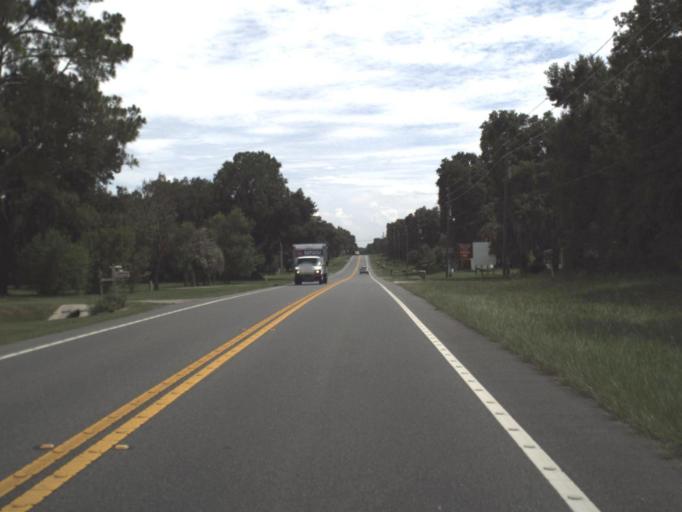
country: US
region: Florida
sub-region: Citrus County
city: Hernando
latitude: 28.9500
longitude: -82.3776
